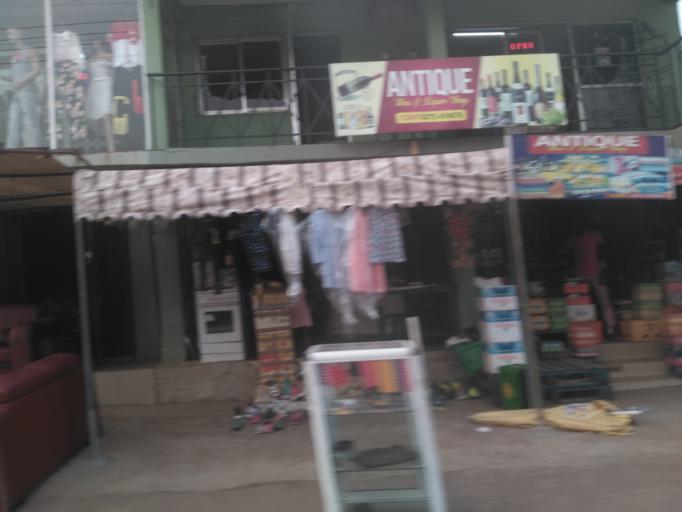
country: GH
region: Ashanti
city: Kumasi
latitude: 6.7081
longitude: -1.6061
